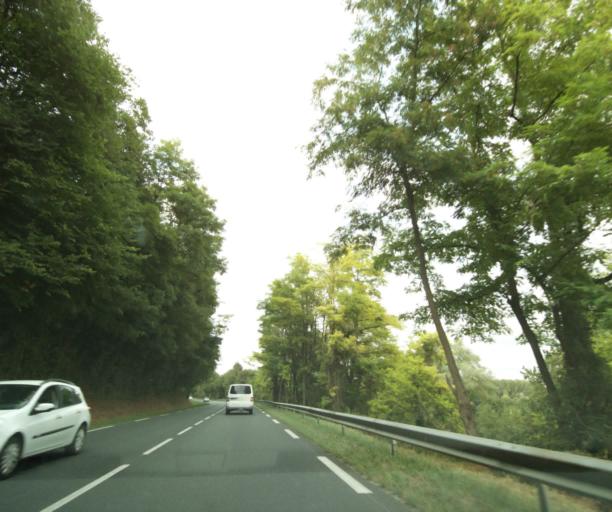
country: FR
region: Centre
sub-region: Departement de l'Indre
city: Clion
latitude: 46.9553
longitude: 1.2159
